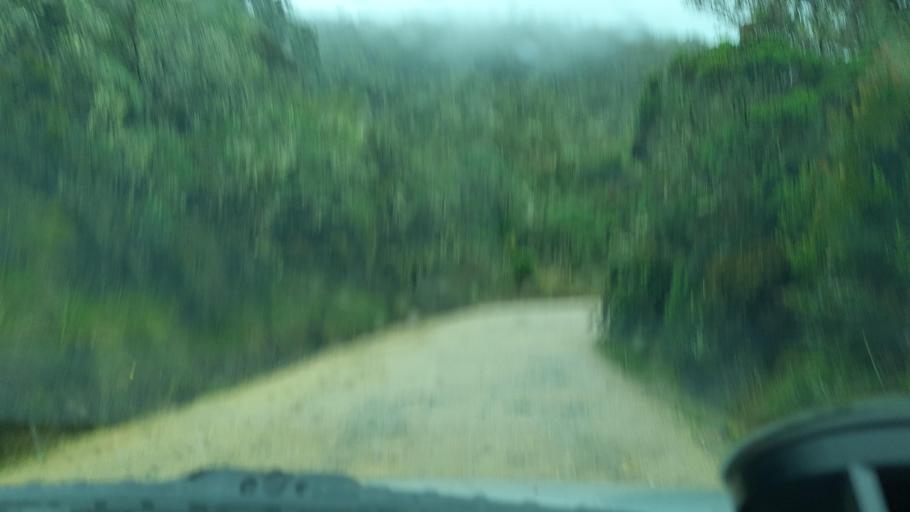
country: CO
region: Cundinamarca
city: Villapinzon
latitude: 5.2145
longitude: -73.5427
